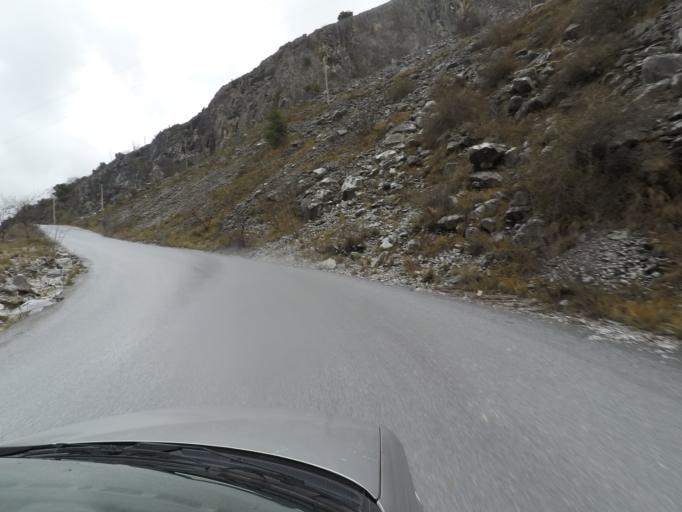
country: IT
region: Tuscany
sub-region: Provincia di Massa-Carrara
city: Massa
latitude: 44.0891
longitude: 10.1316
